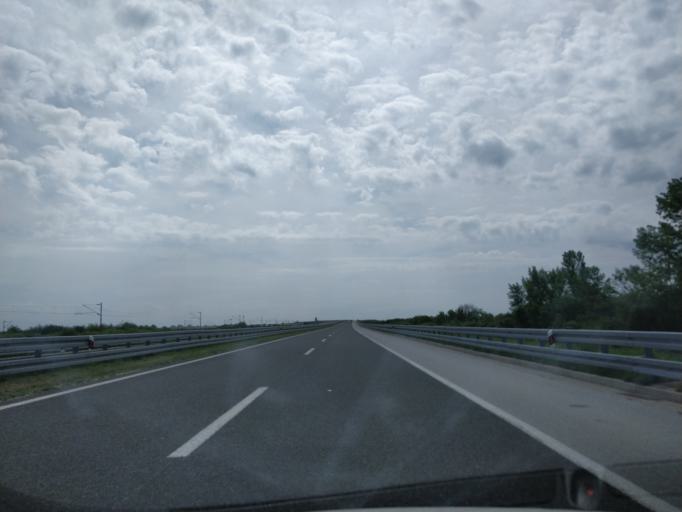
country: HR
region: Zagrebacka
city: Gradici
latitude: 45.7200
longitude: 16.0298
